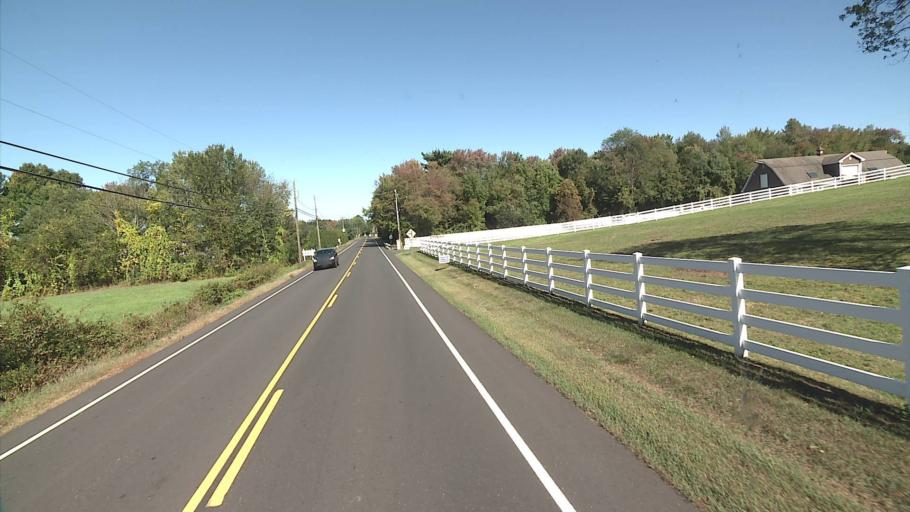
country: US
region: Connecticut
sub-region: Tolland County
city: Somers
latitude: 42.0270
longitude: -72.4531
